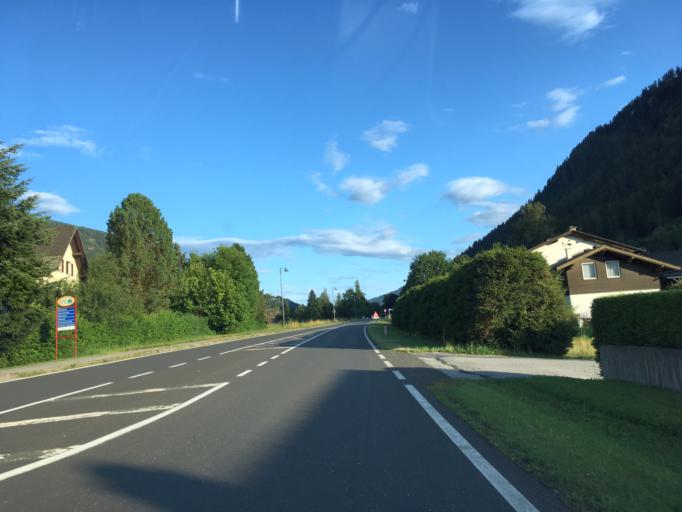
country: AT
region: Carinthia
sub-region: Politischer Bezirk Villach Land
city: Feld am See
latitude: 46.7790
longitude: 13.7427
